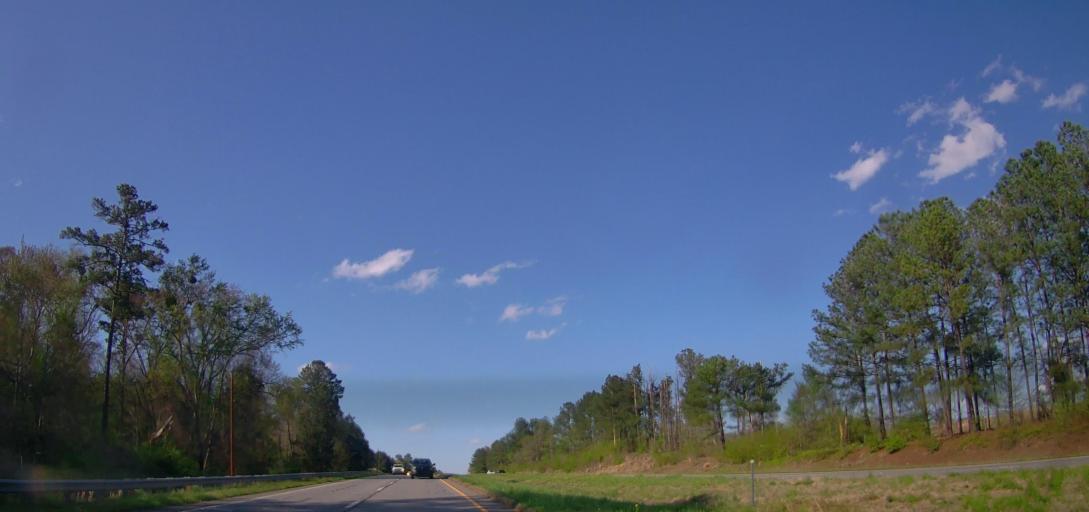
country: US
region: Georgia
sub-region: Baldwin County
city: Hardwick
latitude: 33.0461
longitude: -83.2556
